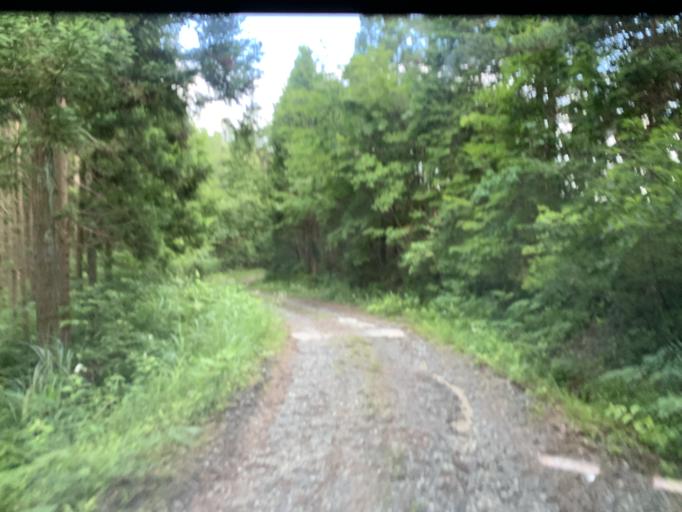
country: JP
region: Iwate
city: Ichinoseki
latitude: 38.9025
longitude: 140.9526
